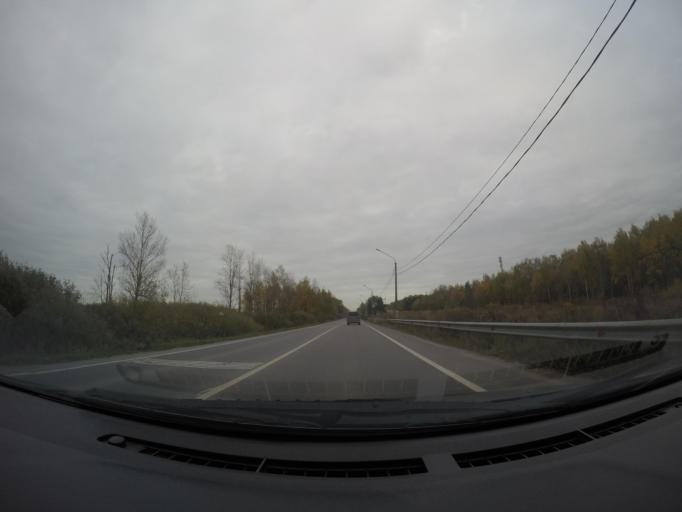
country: RU
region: Moskovskaya
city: Imeni Vorovskogo
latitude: 55.7221
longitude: 38.3705
